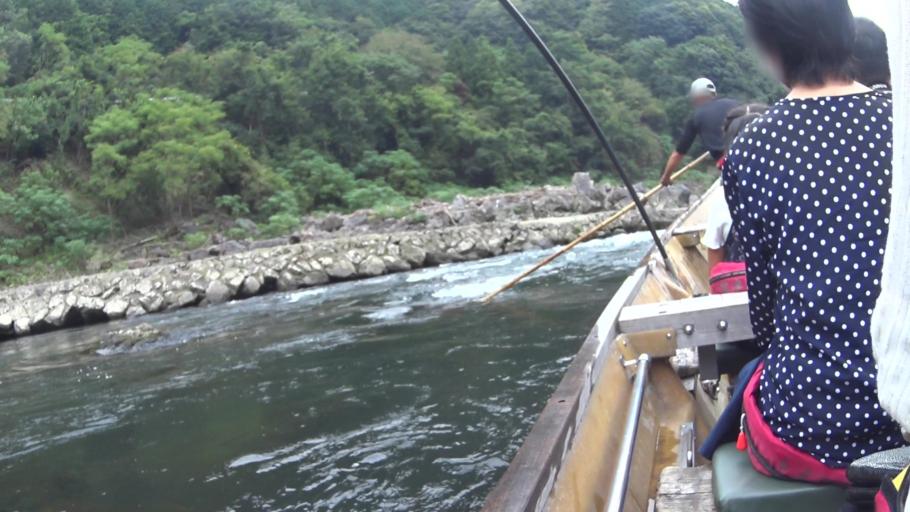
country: JP
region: Kyoto
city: Kameoka
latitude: 35.0234
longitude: 135.6208
